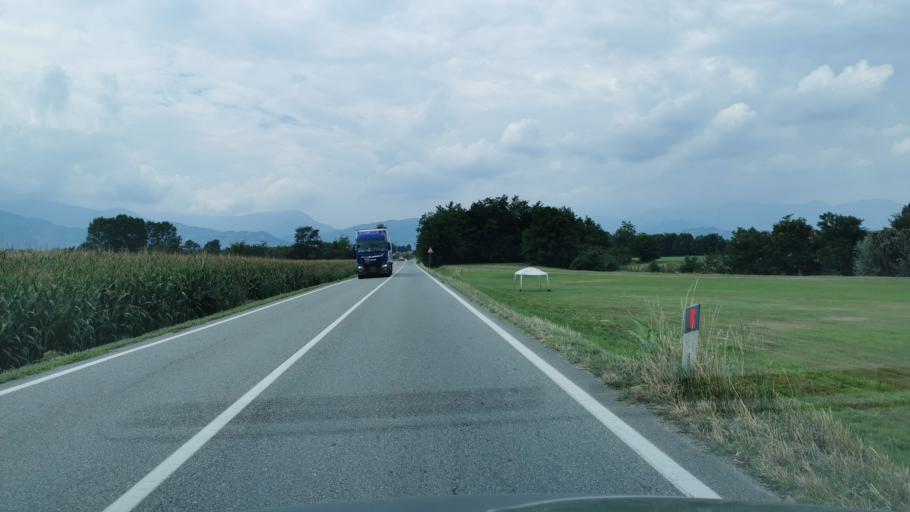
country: IT
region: Piedmont
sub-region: Provincia di Torino
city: Garzigliana
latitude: 44.8339
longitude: 7.3627
